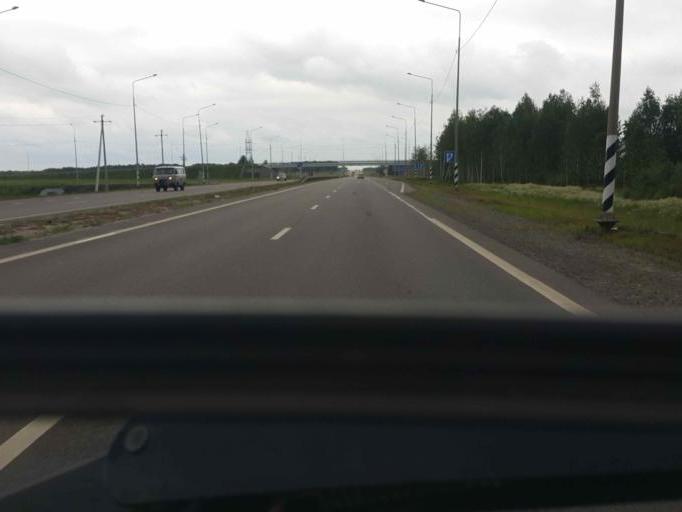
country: RU
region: Tambov
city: Zavoronezhskoye
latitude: 52.8861
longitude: 40.7158
